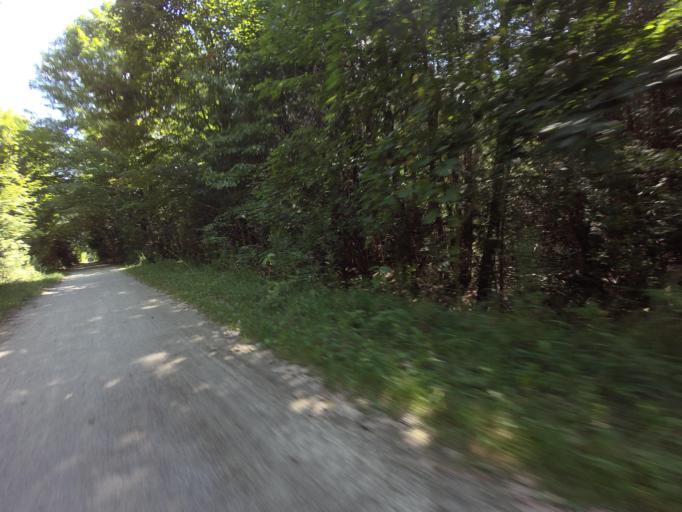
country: CA
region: Ontario
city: Orangeville
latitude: 43.7751
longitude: -80.1027
